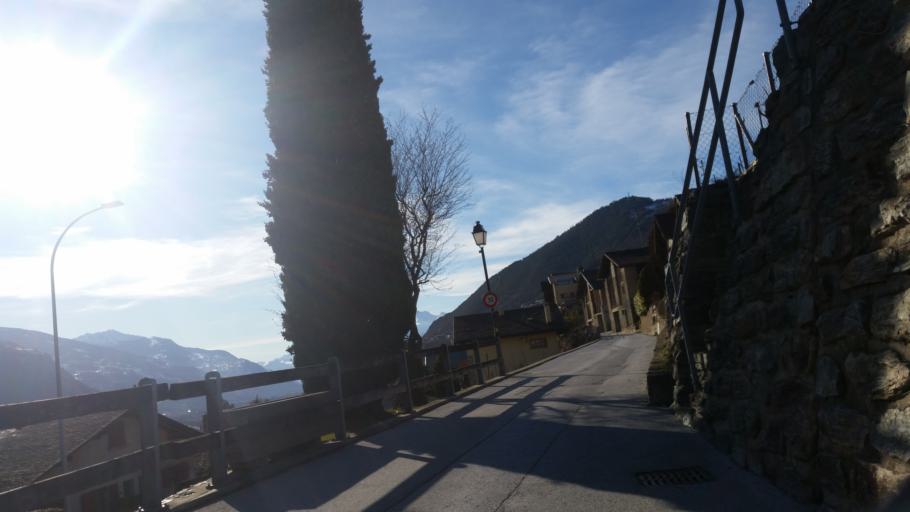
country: CH
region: Valais
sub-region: Sierre District
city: Chermignon-d'en Haut
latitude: 46.2747
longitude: 7.4807
